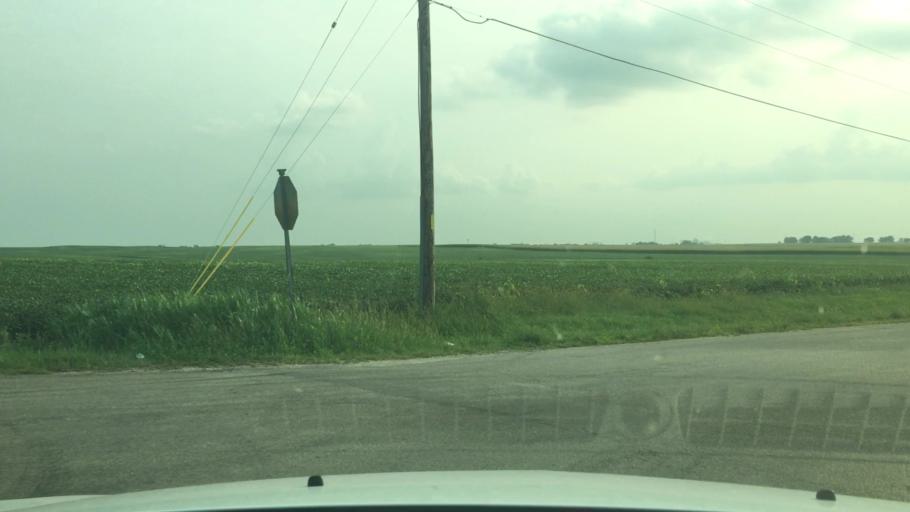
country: US
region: Illinois
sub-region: Ogle County
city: Rochelle
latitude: 41.9204
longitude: -88.9807
